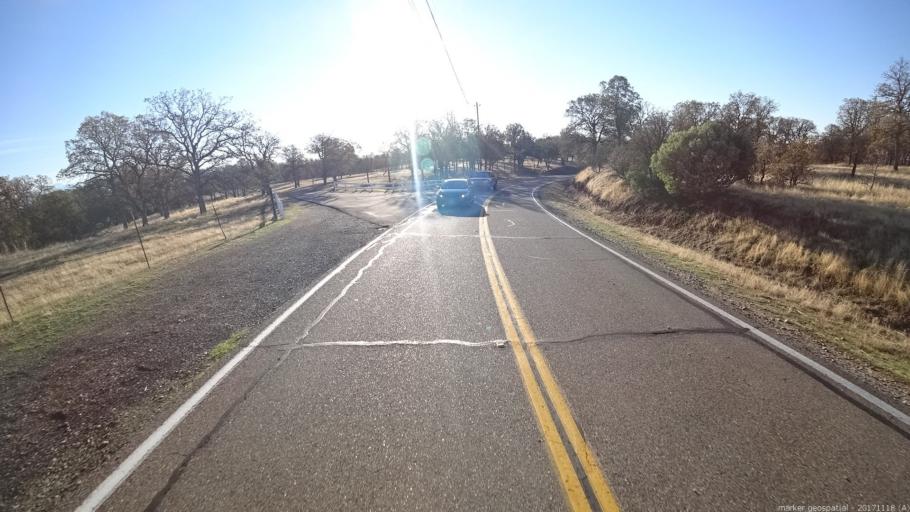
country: US
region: California
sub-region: Shasta County
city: Cottonwood
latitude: 40.4164
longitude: -122.2836
